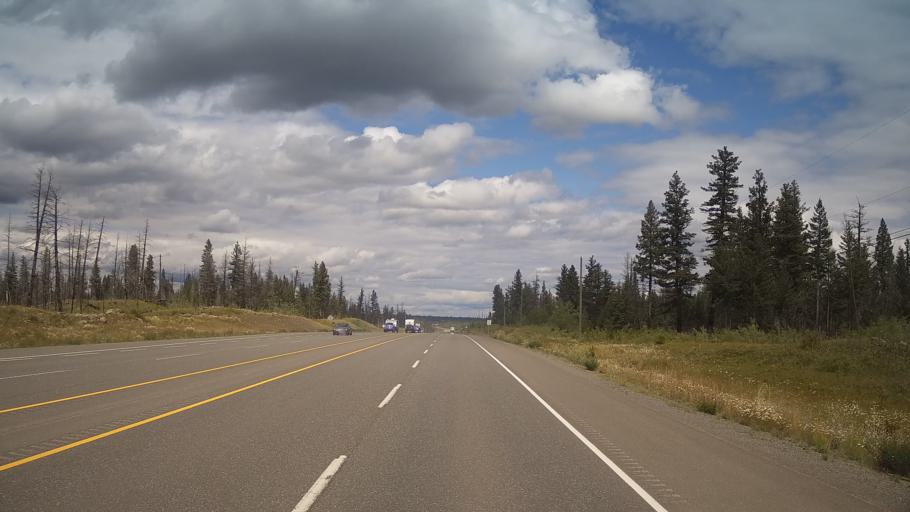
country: CA
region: British Columbia
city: Cache Creek
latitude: 51.3291
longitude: -121.3847
